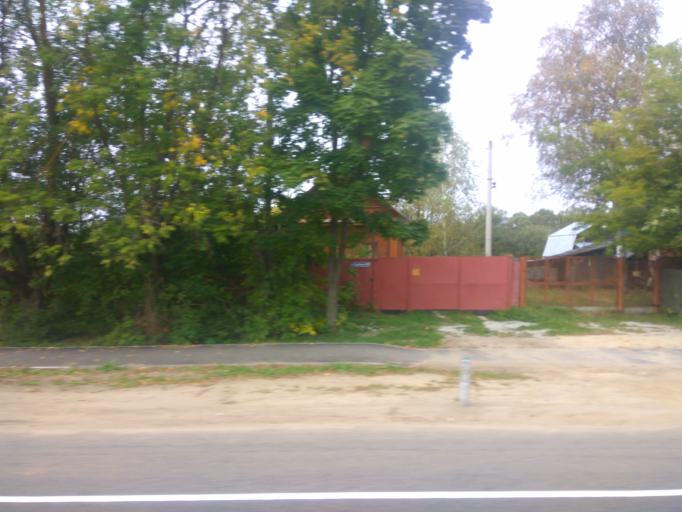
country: RU
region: Moskovskaya
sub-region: Shchelkovskiy Rayon
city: Grebnevo
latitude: 55.9900
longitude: 38.1269
